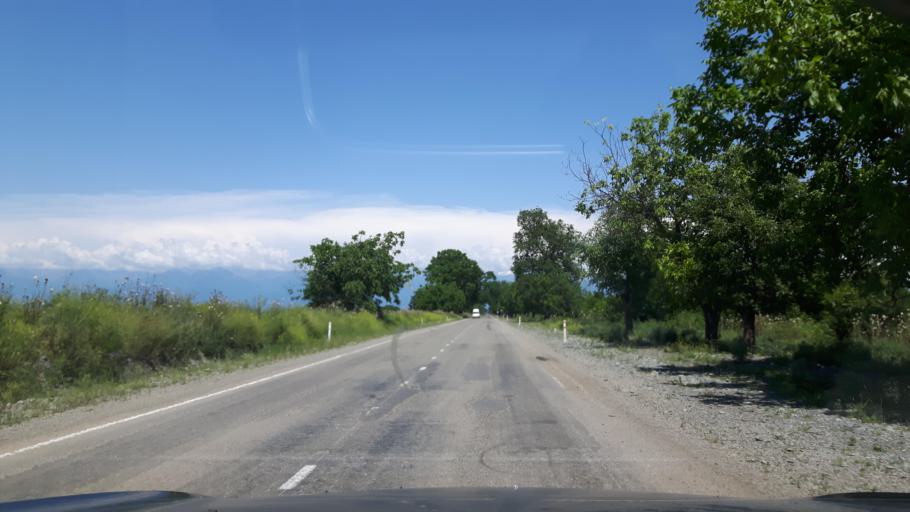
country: GE
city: Tsnori
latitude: 41.6315
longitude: 46.0226
